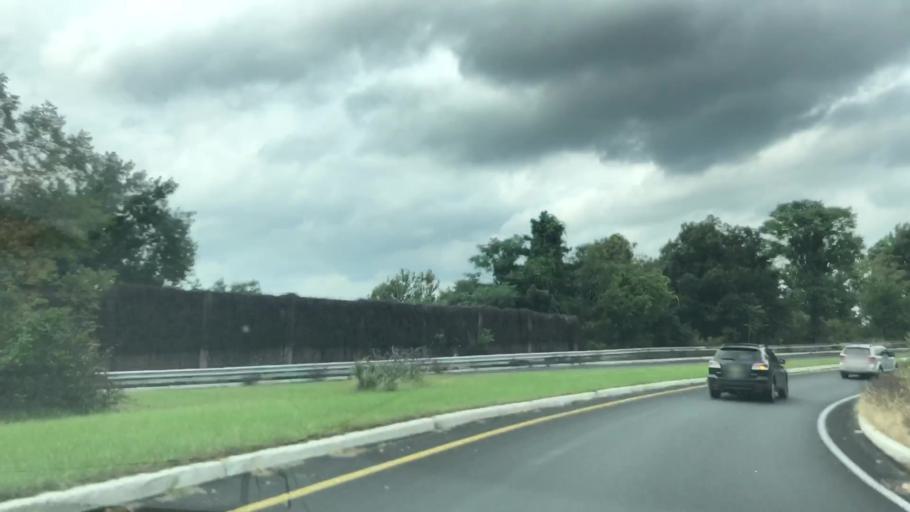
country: US
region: New Jersey
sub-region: Essex County
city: West Orange
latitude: 40.7986
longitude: -74.2537
